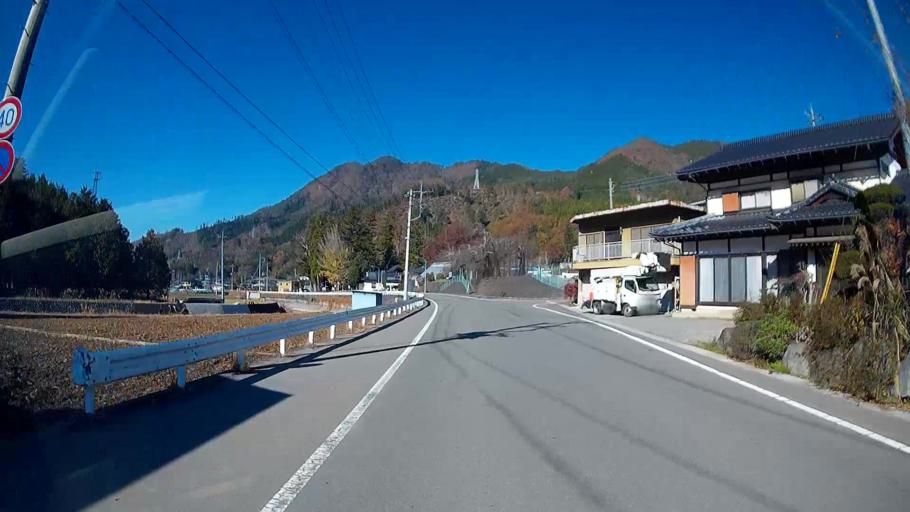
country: JP
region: Yamanashi
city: Otsuki
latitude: 35.5623
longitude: 138.9749
